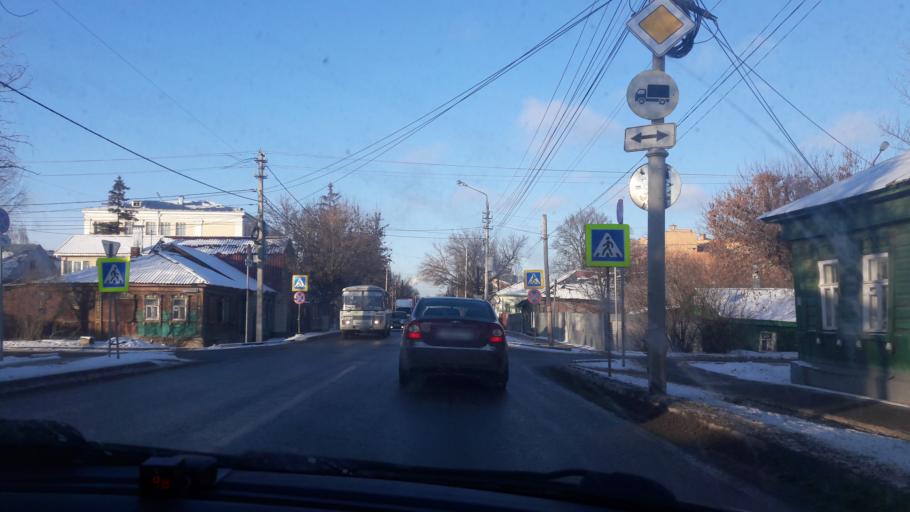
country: RU
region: Tula
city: Tula
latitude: 54.1854
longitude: 37.6272
